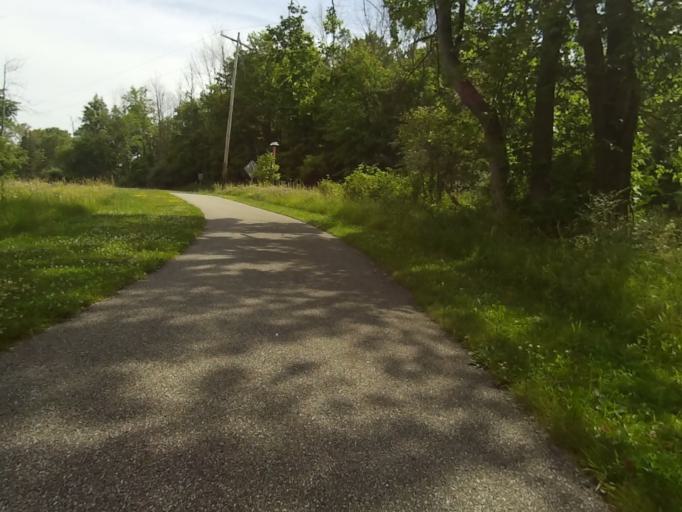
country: US
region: Ohio
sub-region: Summit County
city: Boston Heights
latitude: 41.2796
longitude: -81.5383
